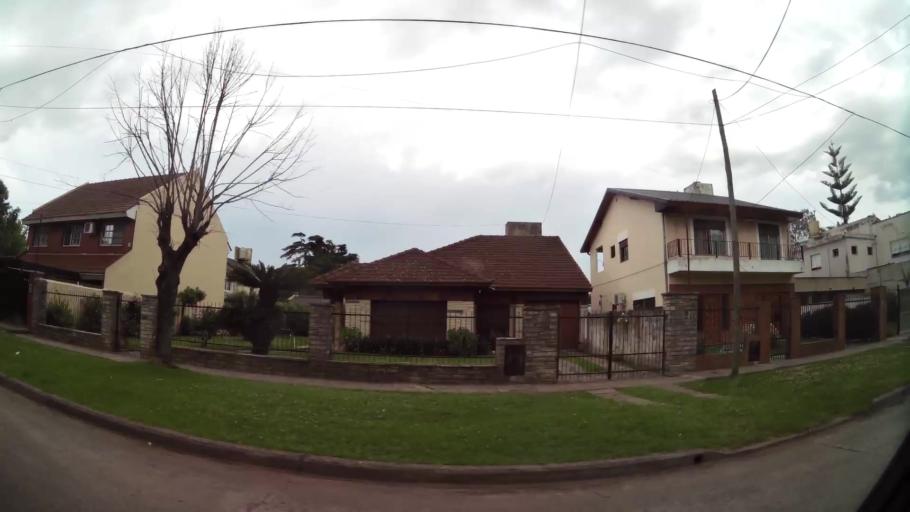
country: AR
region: Buenos Aires
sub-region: Partido de Tigre
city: Tigre
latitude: -34.4664
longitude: -58.6504
